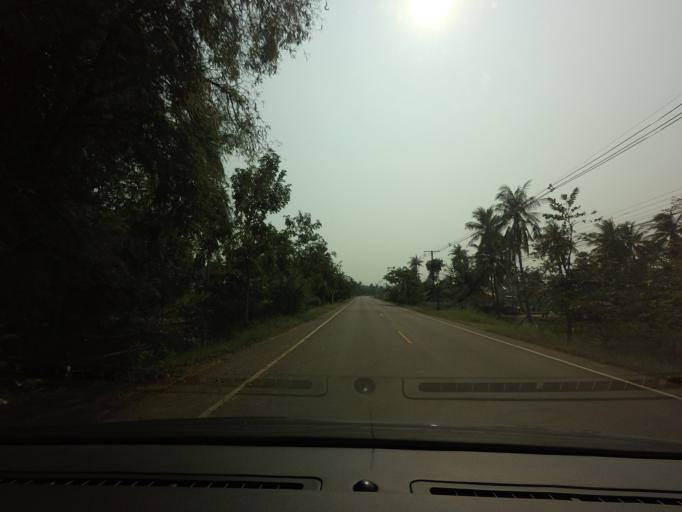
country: TH
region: Prachuap Khiri Khan
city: Kui Buri
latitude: 12.0366
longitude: 99.9005
